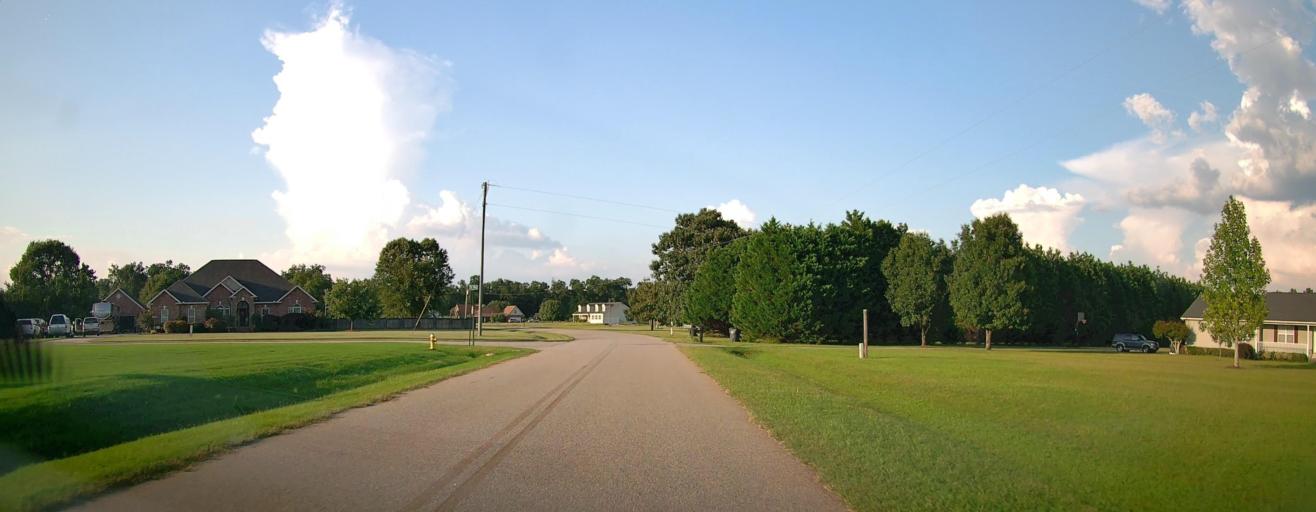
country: US
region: Georgia
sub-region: Peach County
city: Byron
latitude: 32.6482
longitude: -83.7912
